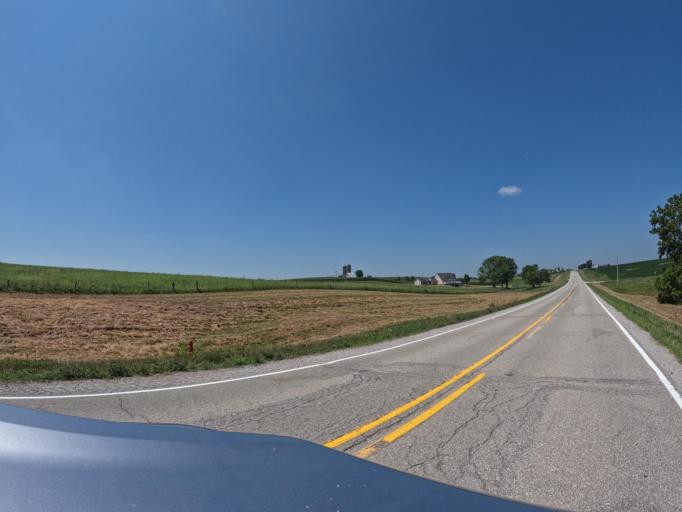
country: US
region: Iowa
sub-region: Keokuk County
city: Sigourney
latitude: 41.2650
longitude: -92.2175
